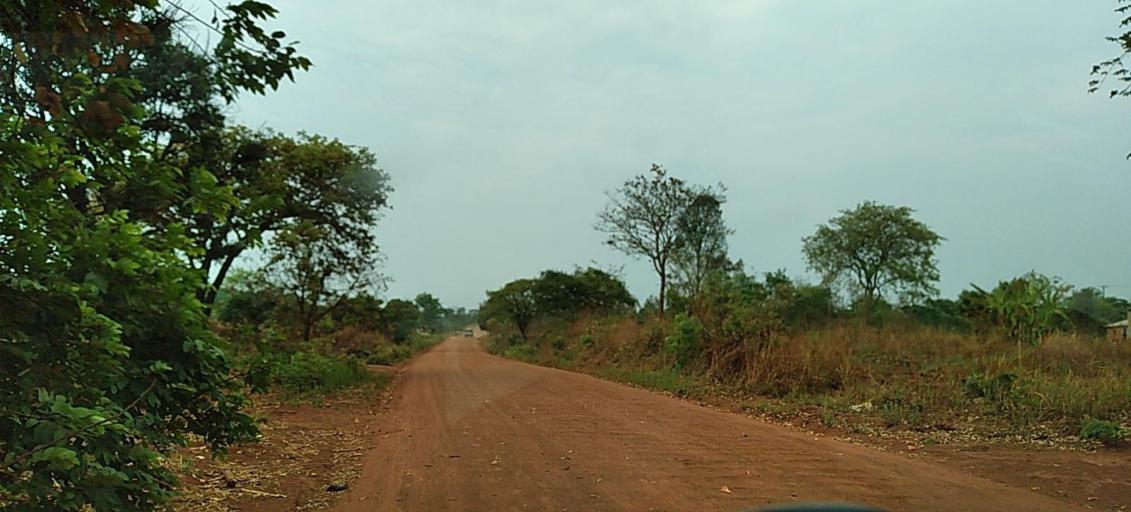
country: ZM
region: North-Western
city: Solwezi
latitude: -12.2286
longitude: 26.5108
